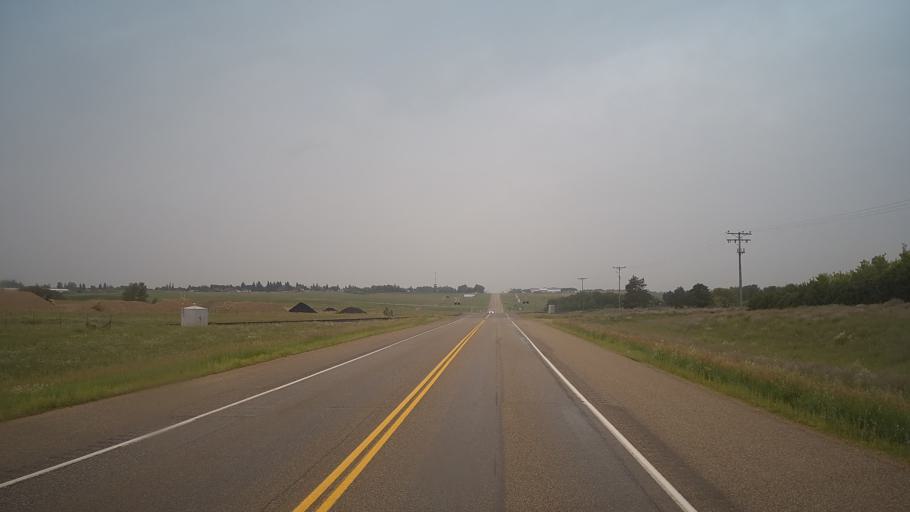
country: CA
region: Saskatchewan
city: Biggar
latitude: 52.0572
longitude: -107.9536
